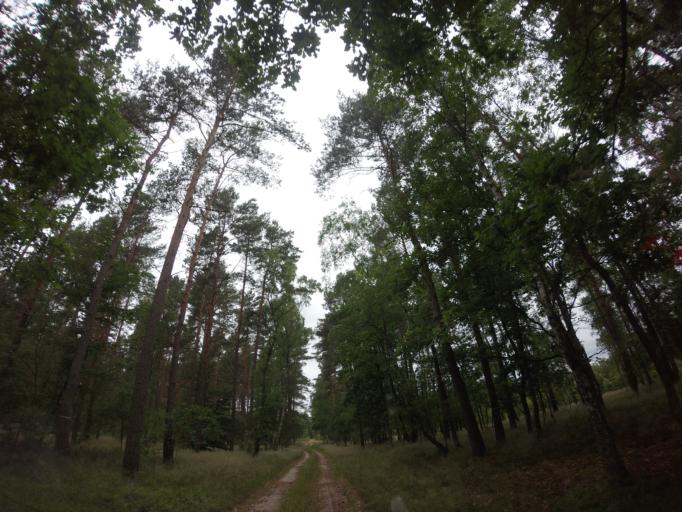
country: PL
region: West Pomeranian Voivodeship
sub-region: Powiat choszczenski
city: Drawno
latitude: 53.1458
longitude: 15.7099
